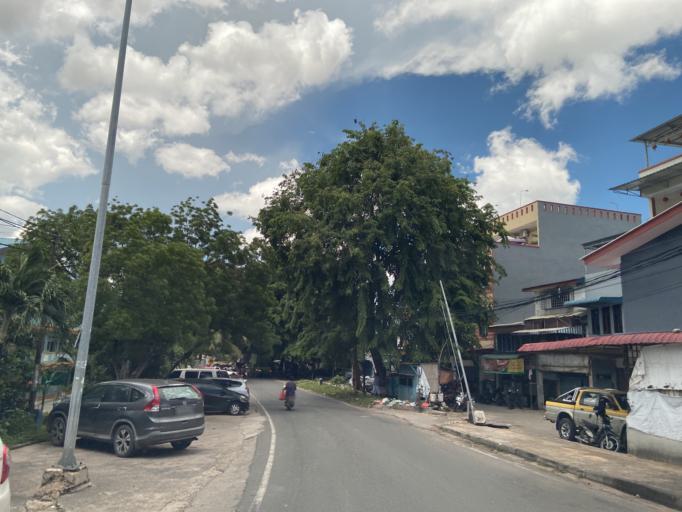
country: SG
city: Singapore
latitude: 1.1375
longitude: 104.0124
